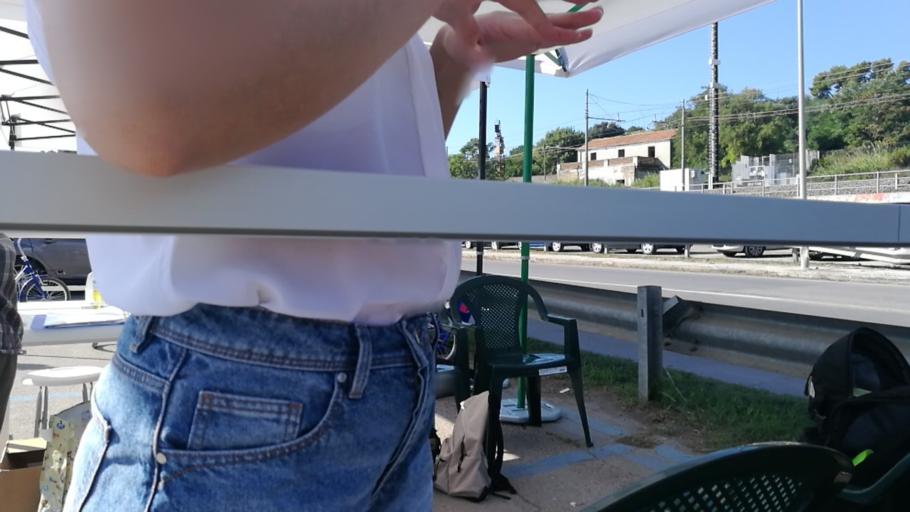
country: IT
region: Abruzzo
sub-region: Provincia di Chieti
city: Ortona
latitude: 42.3458
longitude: 14.4102
